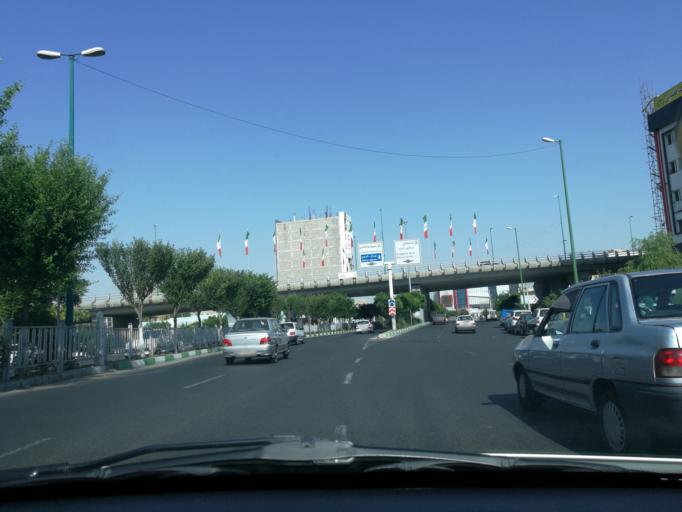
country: IR
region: Alborz
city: Karaj
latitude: 35.8416
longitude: 50.9829
